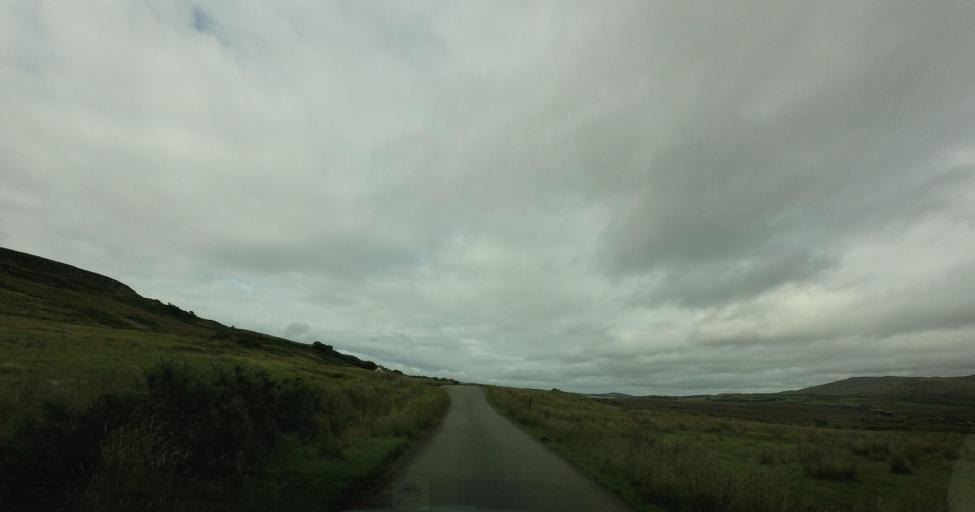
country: GB
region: Scotland
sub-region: Highland
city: Portree
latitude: 57.4154
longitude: -6.2199
